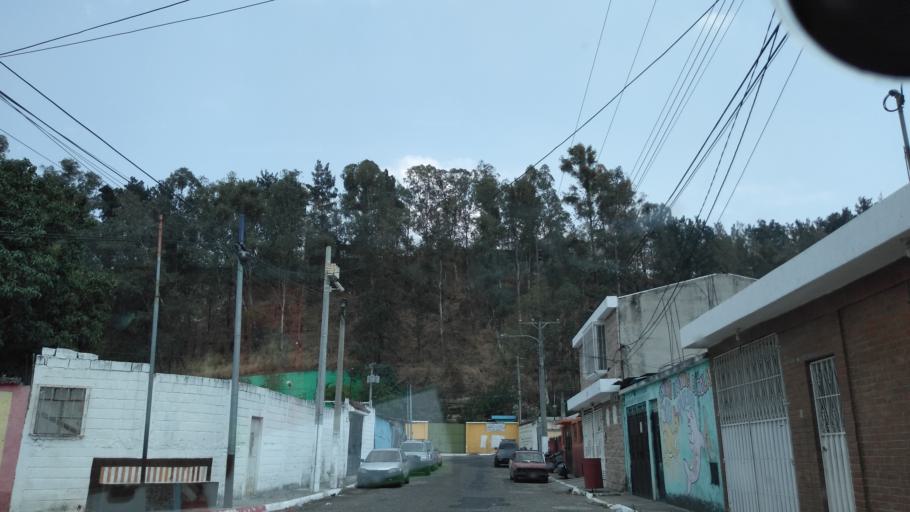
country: GT
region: Guatemala
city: Petapa
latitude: 14.5238
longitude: -90.5423
